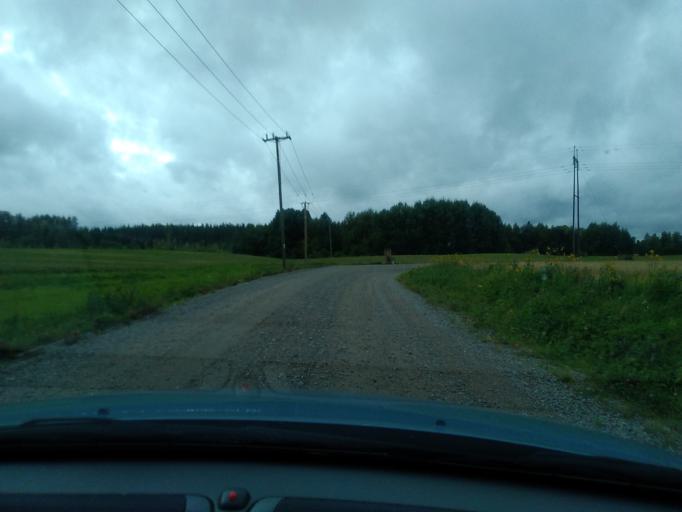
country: FI
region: Central Finland
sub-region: Saarijaervi-Viitasaari
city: Saarijaervi
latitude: 62.6935
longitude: 25.3358
